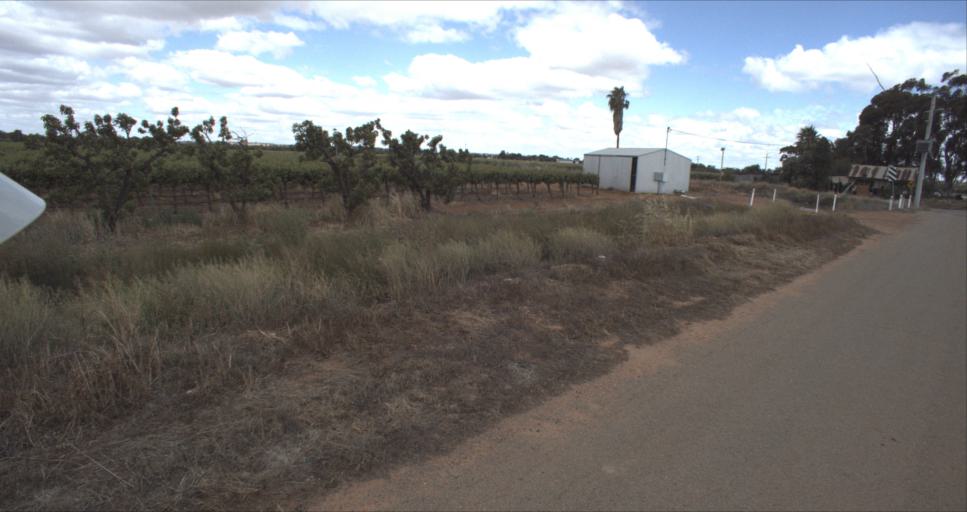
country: AU
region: New South Wales
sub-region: Leeton
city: Leeton
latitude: -34.5794
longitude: 146.4003
